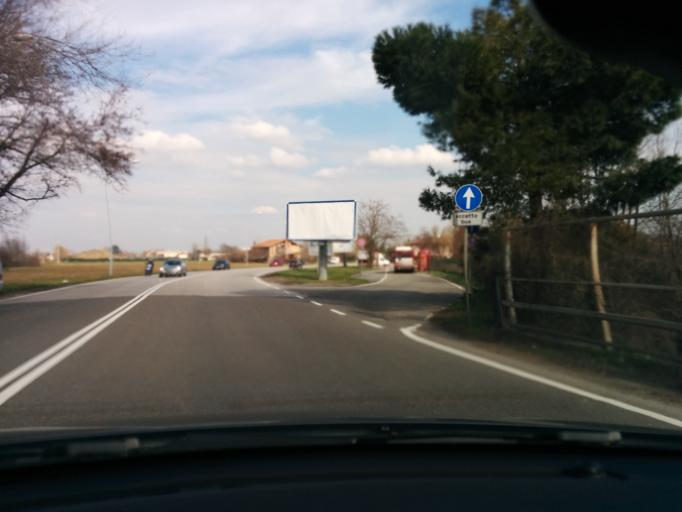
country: IT
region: Emilia-Romagna
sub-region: Provincia di Bologna
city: Trebbo
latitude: 44.5320
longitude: 11.3358
